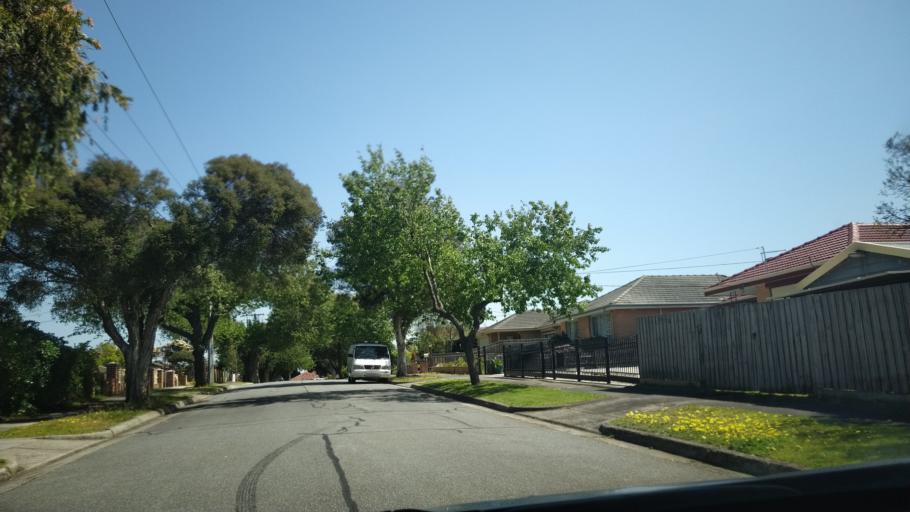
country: AU
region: Victoria
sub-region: Greater Dandenong
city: Noble Park
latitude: -37.9708
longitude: 145.1648
